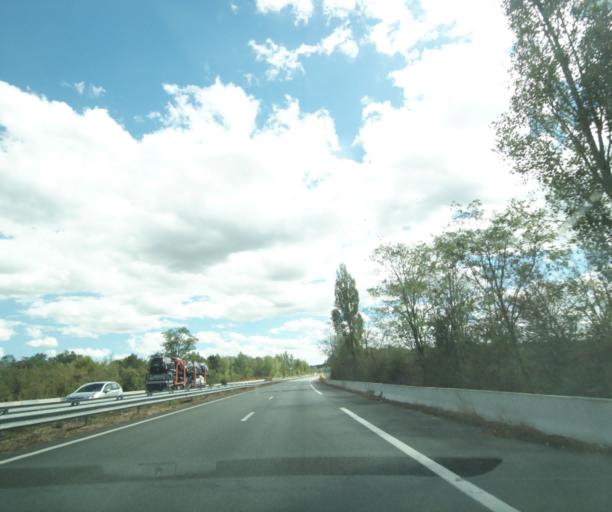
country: FR
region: Aquitaine
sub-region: Departement de la Gironde
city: Gironde-sur-Dropt
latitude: 44.5307
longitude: -0.0933
